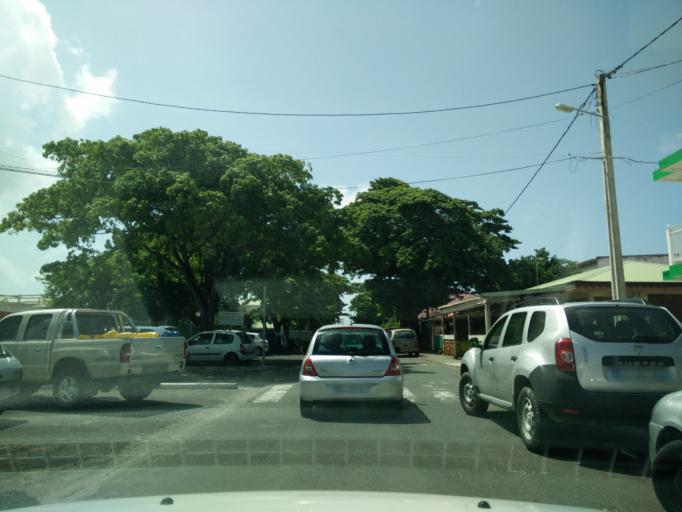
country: GP
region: Guadeloupe
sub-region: Guadeloupe
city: Grand-Bourg
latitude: 15.8817
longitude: -61.3138
